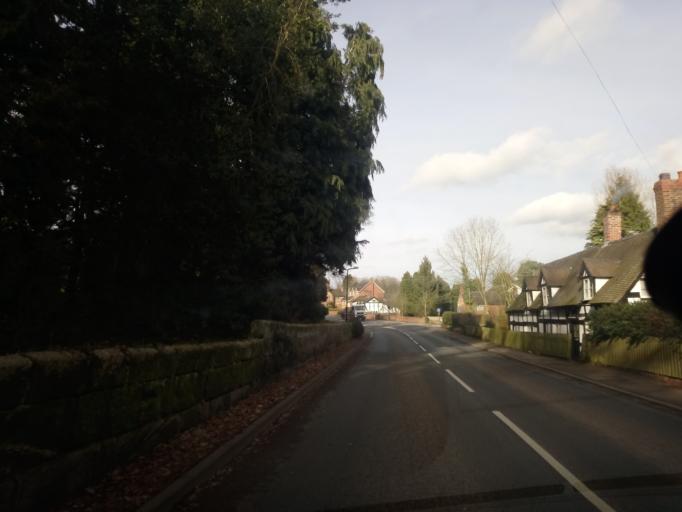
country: GB
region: England
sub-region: Shropshire
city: Stoke upon Tern
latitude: 52.8508
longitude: -2.5734
